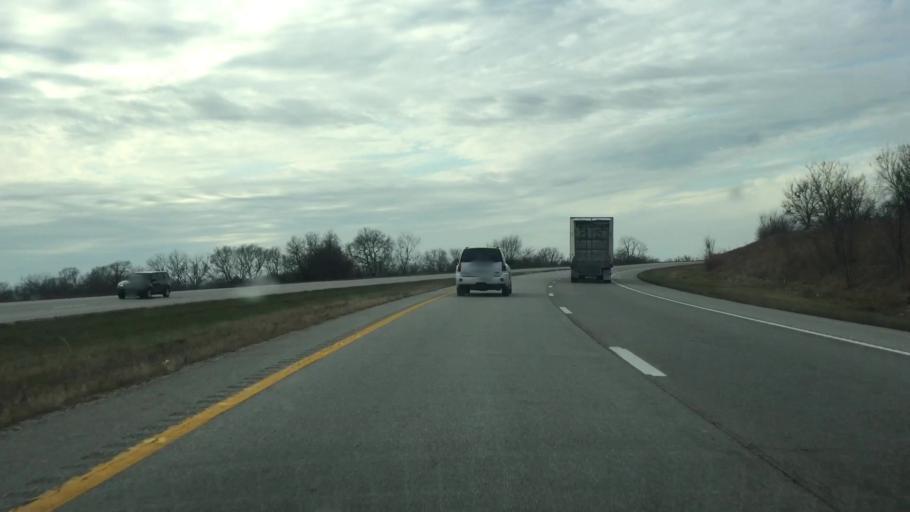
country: US
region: Missouri
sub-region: Cass County
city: Garden City
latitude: 38.5181
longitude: -94.1371
